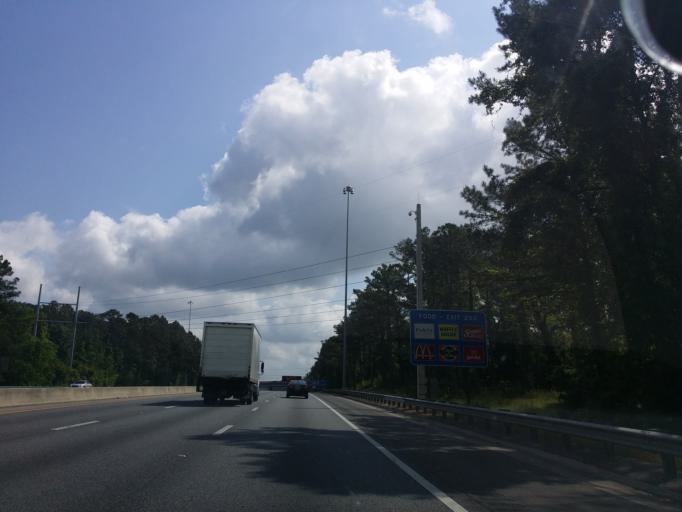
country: US
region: Florida
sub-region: Leon County
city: Tallahassee
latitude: 30.4919
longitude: -84.2806
